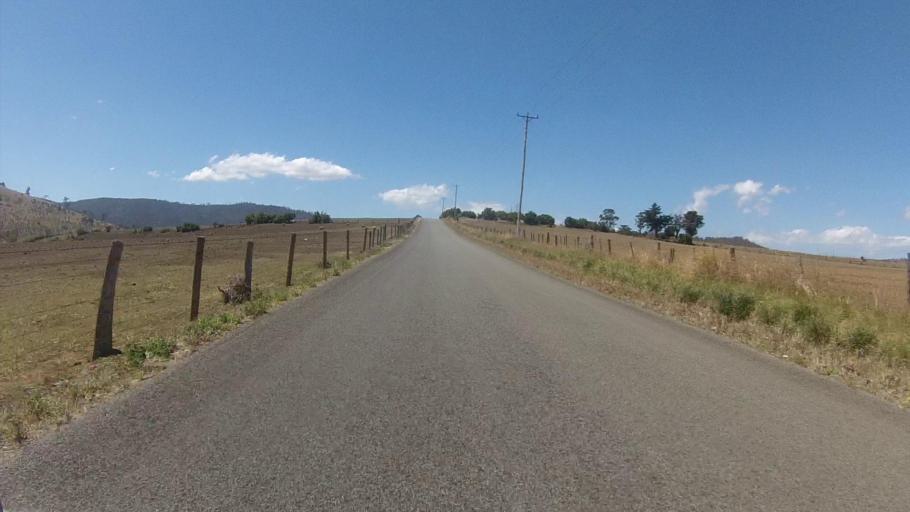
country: AU
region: Tasmania
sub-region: Sorell
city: Sorell
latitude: -42.7689
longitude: 147.5968
